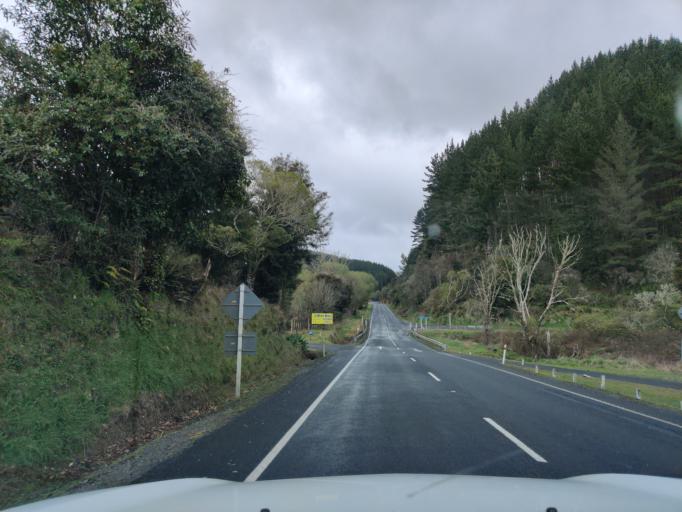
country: NZ
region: Waikato
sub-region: Otorohanga District
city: Otorohanga
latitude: -38.6530
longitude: 175.2079
